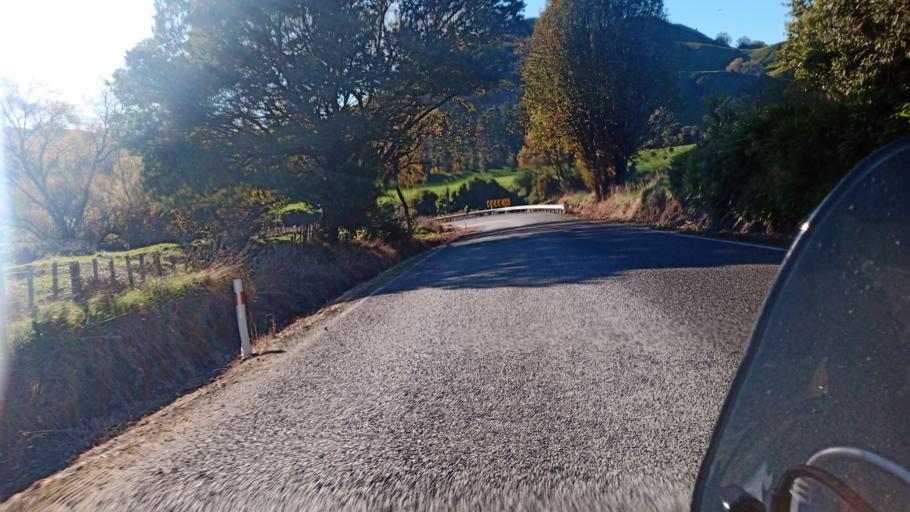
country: NZ
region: Hawke's Bay
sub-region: Wairoa District
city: Wairoa
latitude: -38.8712
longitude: 177.2117
